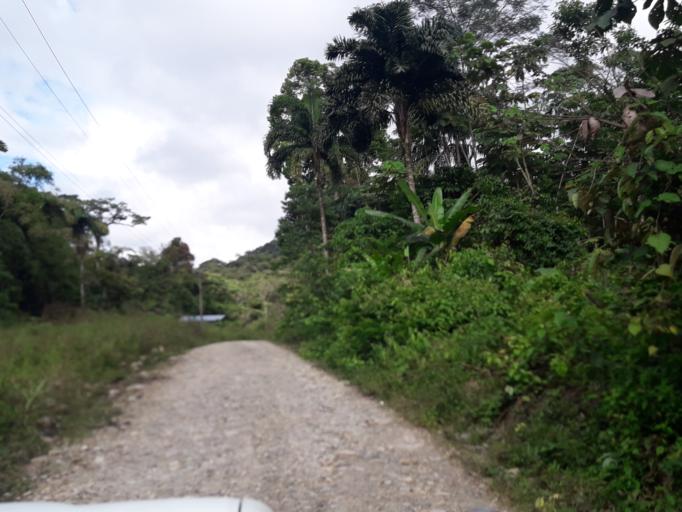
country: EC
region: Napo
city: Archidona
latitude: -0.9451
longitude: -77.8891
